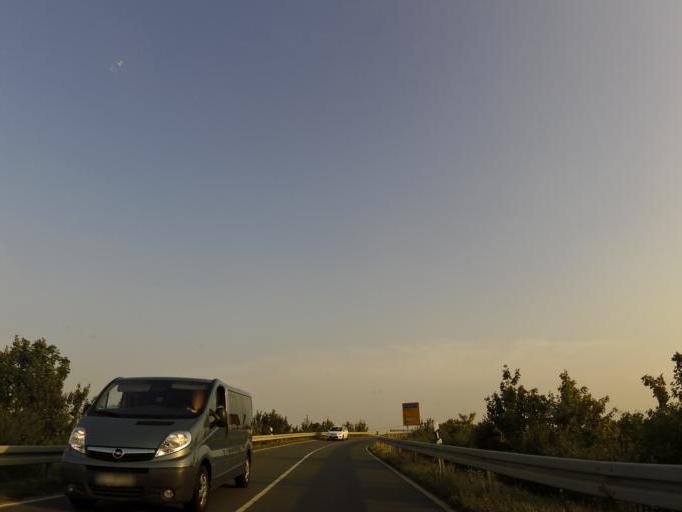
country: DE
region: Hesse
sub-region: Regierungsbezirk Darmstadt
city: Buttelborn
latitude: 49.9191
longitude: 8.5281
